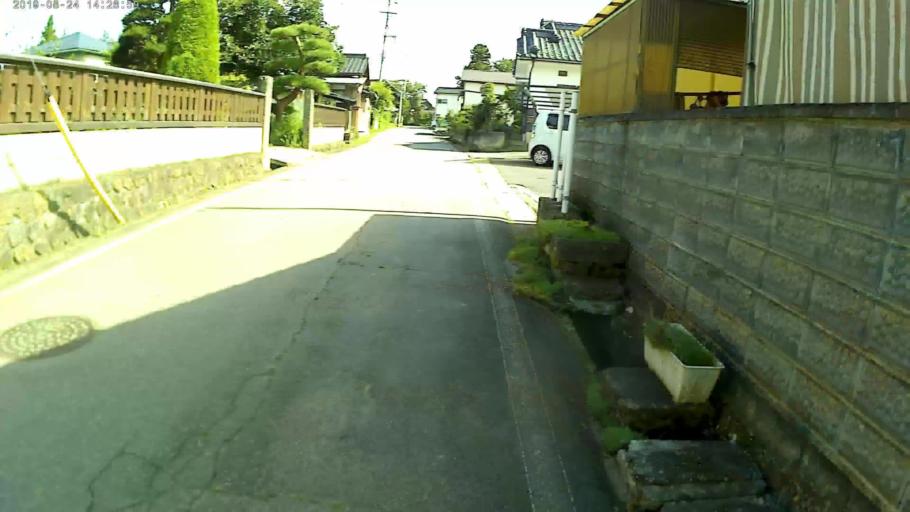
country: JP
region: Nagano
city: Komoro
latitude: 36.2686
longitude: 138.4319
